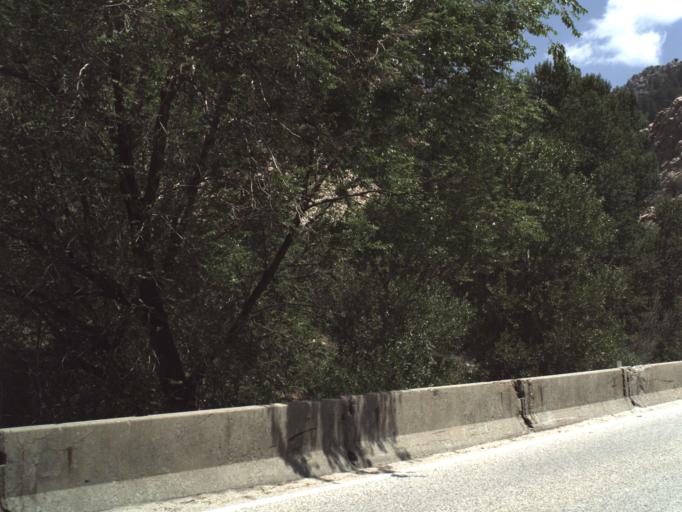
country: US
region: Utah
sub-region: Weber County
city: Ogden
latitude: 41.2372
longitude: -111.9161
